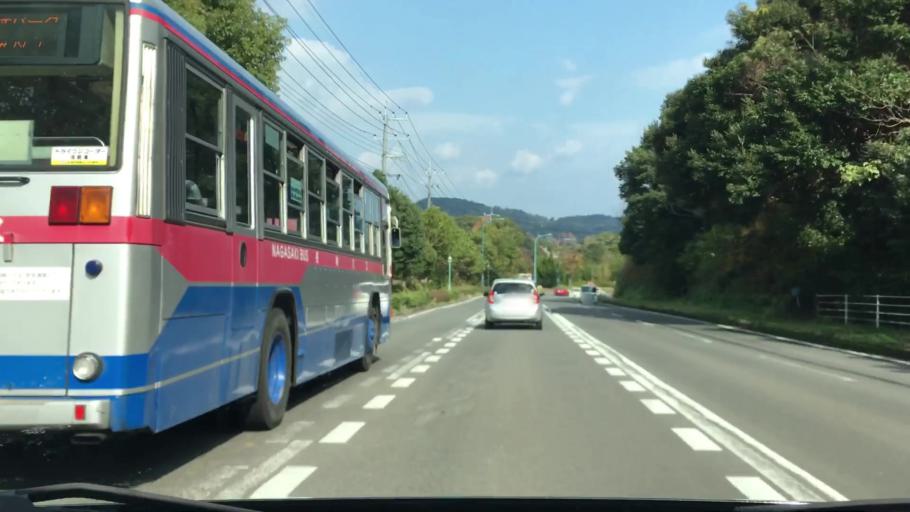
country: JP
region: Nagasaki
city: Sasebo
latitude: 32.9938
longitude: 129.7518
